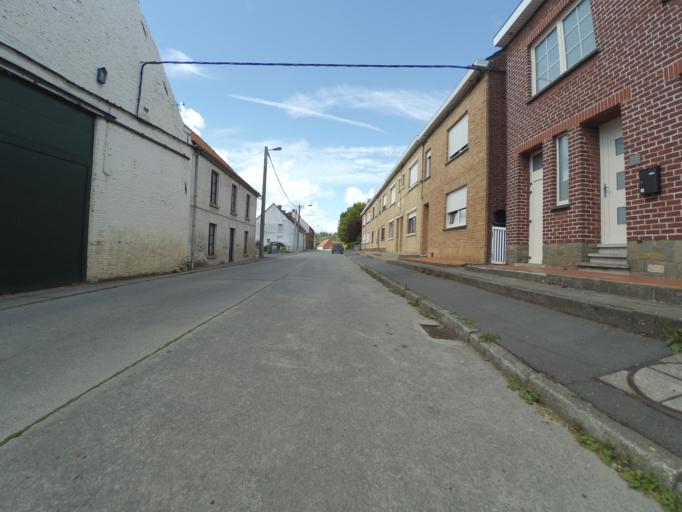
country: BE
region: Wallonia
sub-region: Province du Hainaut
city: Frasnes-lez-Buissenal
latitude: 50.6696
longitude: 3.6171
